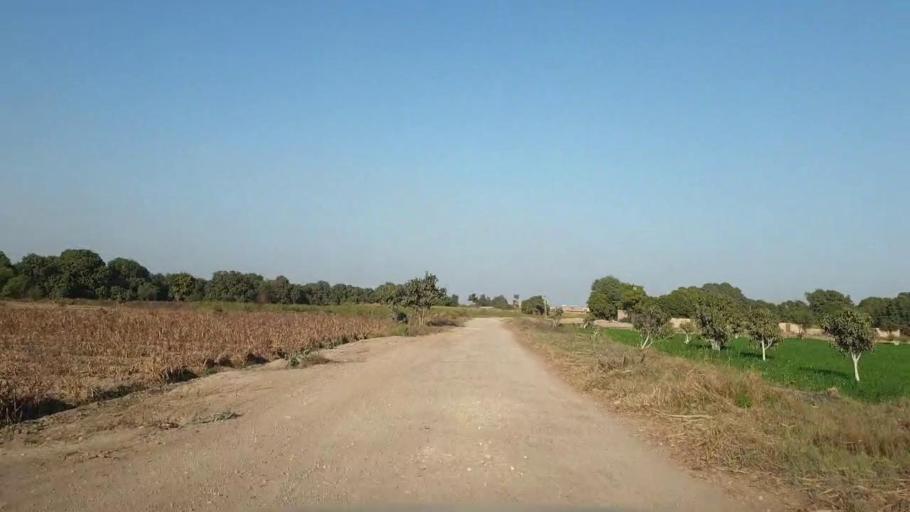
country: PK
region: Sindh
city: Tando Allahyar
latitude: 25.4906
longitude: 68.6412
